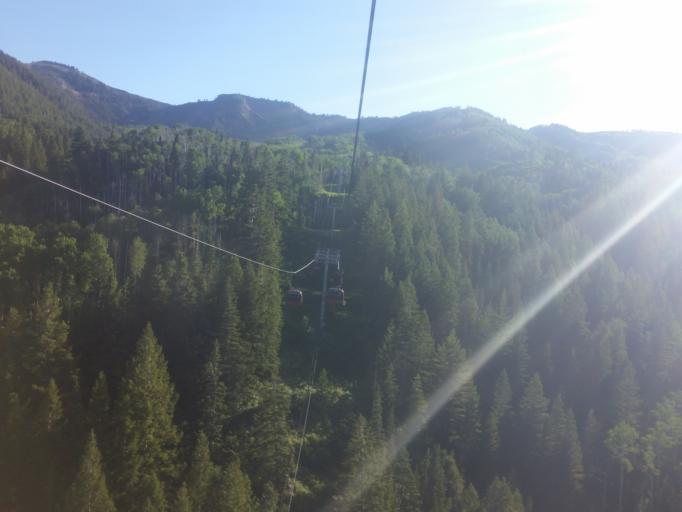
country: US
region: Utah
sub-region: Summit County
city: Snyderville
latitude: 40.6809
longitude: -111.5712
